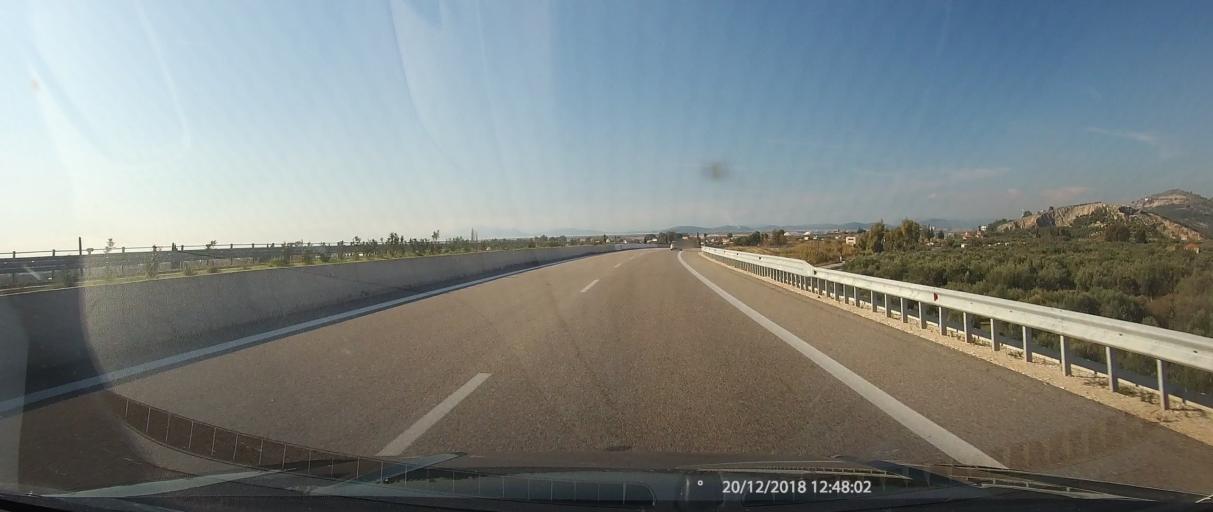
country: GR
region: West Greece
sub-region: Nomos Aitolias kai Akarnanias
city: Mesolongi
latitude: 38.3935
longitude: 21.4305
